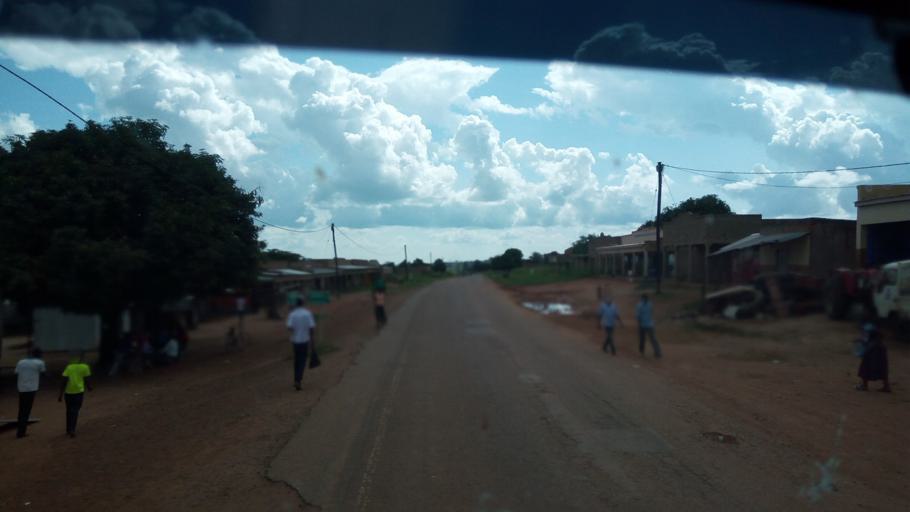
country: UG
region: Northern Region
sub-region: Nwoya District
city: Nwoya
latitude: 2.5371
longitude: 31.8828
